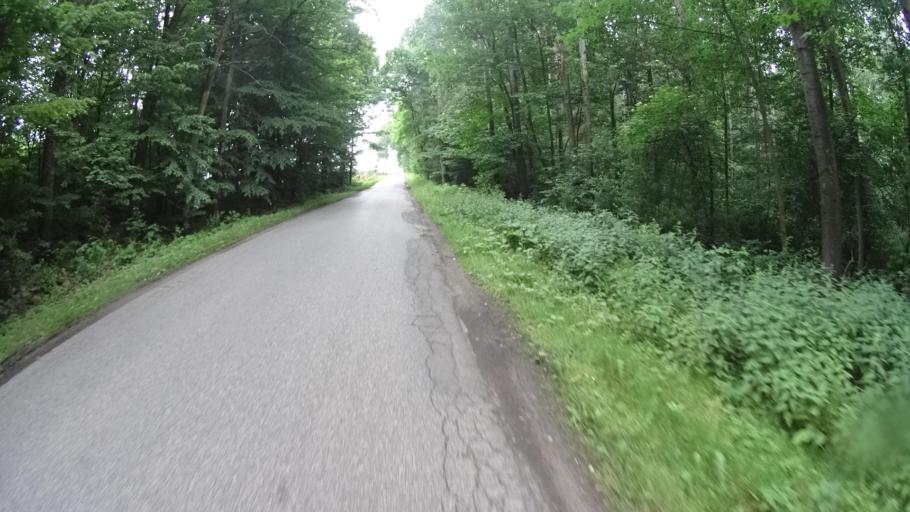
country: PL
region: Masovian Voivodeship
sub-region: Powiat grojecki
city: Goszczyn
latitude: 51.7814
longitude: 20.8539
